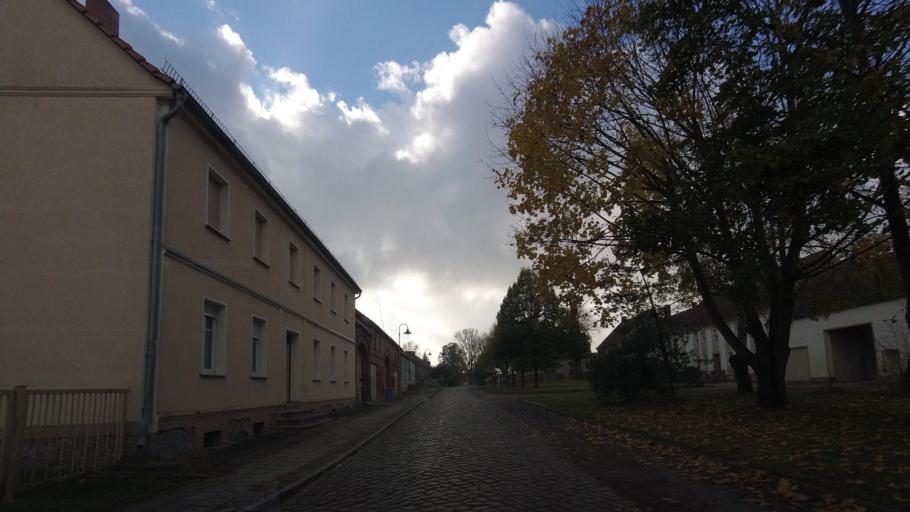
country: DE
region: Brandenburg
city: Niedergorsdorf
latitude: 51.9724
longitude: 12.9673
